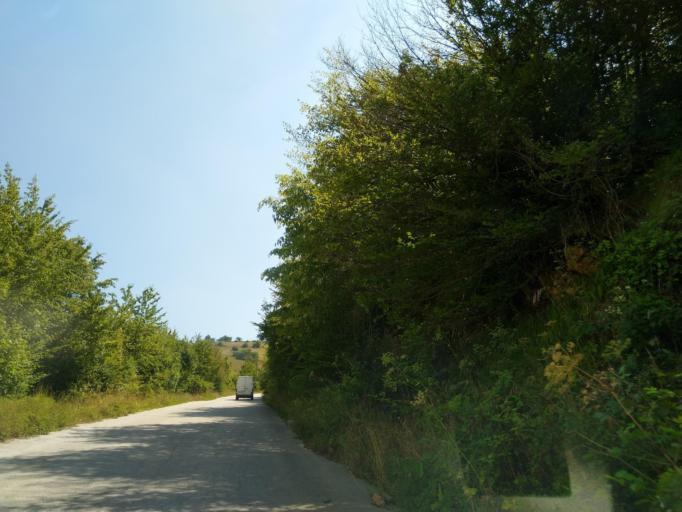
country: RS
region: Central Serbia
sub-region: Zlatiborski Okrug
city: Nova Varos
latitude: 43.4204
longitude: 19.9320
